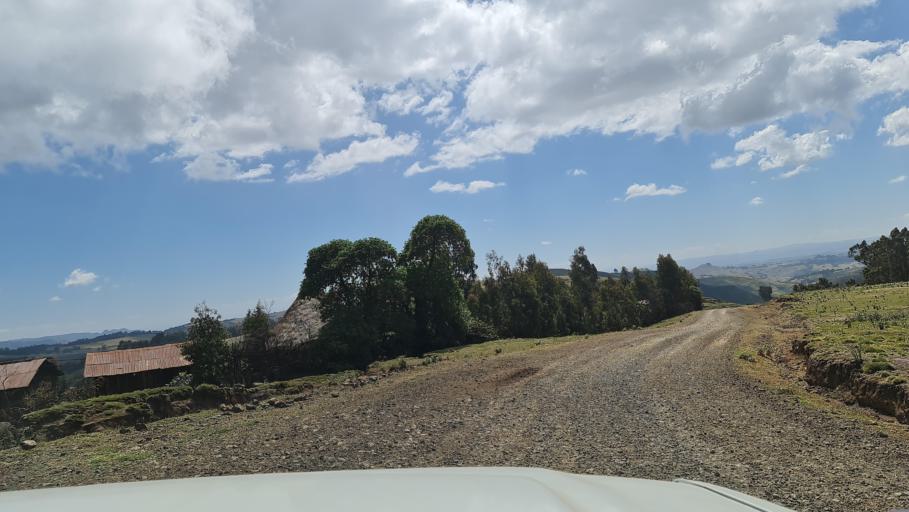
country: ET
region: Amhara
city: Debark'
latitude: 13.2085
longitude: 37.9733
